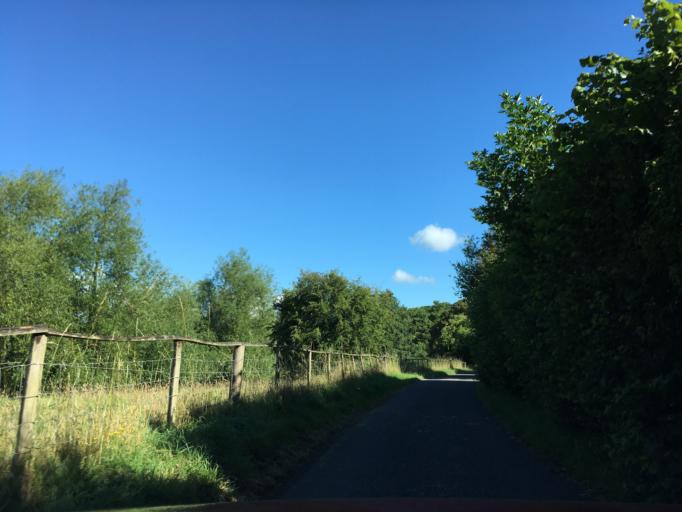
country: GB
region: England
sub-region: Herefordshire
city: Yatton
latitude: 51.9632
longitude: -2.5593
